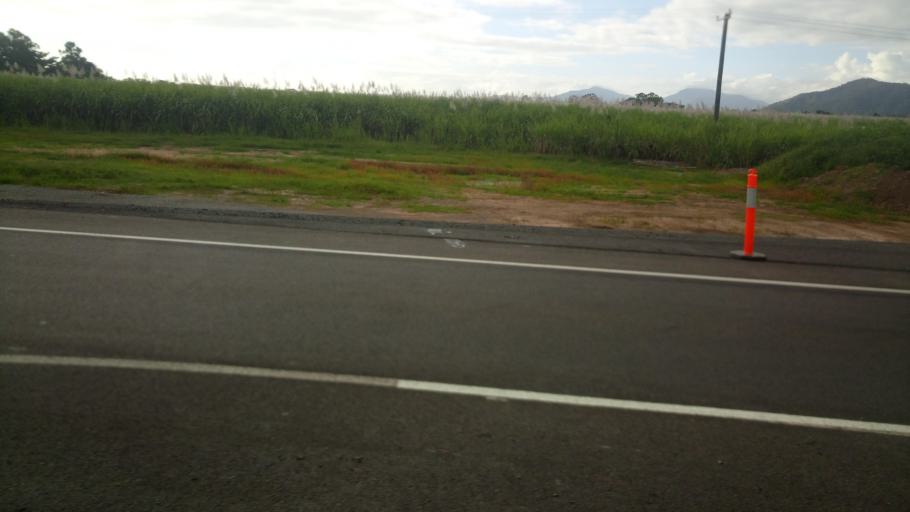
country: AU
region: Queensland
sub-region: Cairns
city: Redlynch
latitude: -16.8498
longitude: 145.6960
